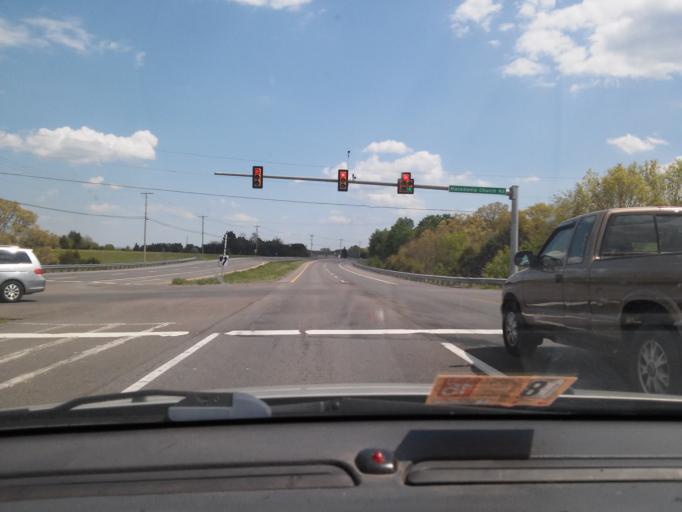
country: US
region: Virginia
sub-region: Frederick County
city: Stephens City
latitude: 39.0977
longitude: -78.1554
